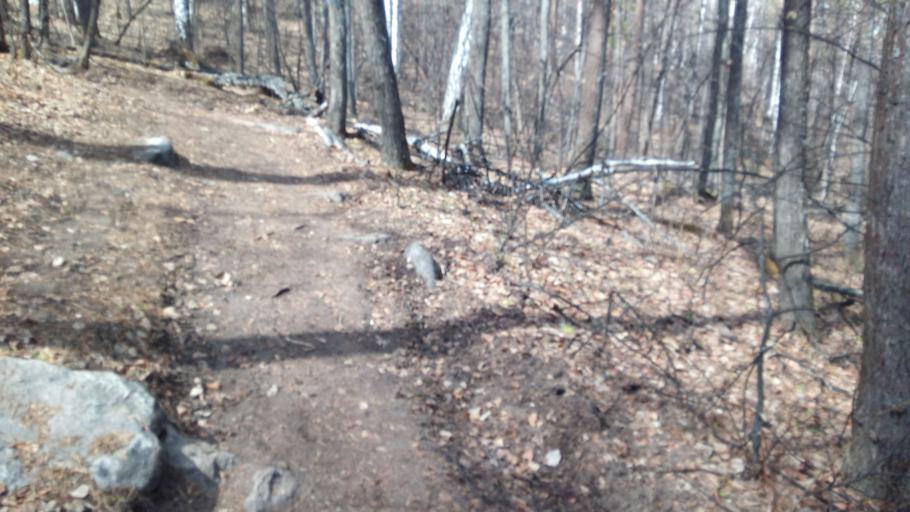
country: RU
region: Chelyabinsk
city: Syrostan
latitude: 55.1664
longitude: 59.9776
